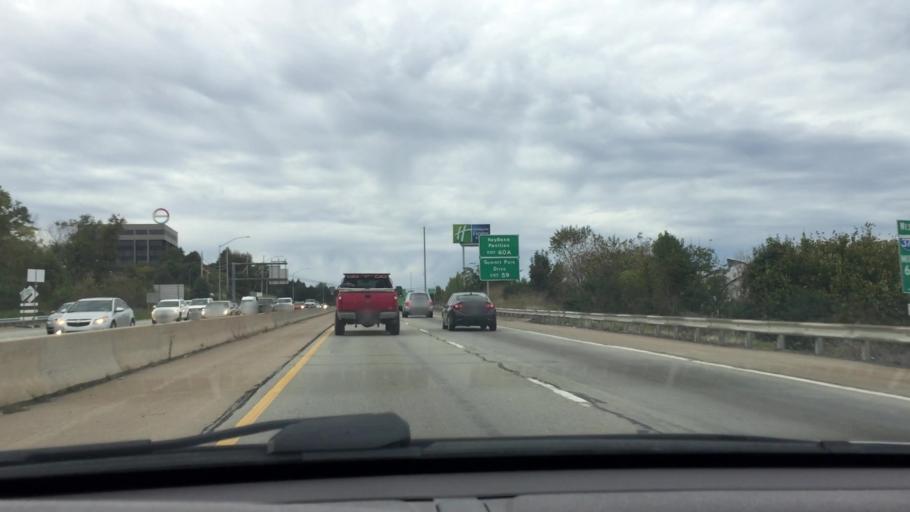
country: US
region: Pennsylvania
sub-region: Allegheny County
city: Rennerdale
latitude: 40.4424
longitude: -80.1596
